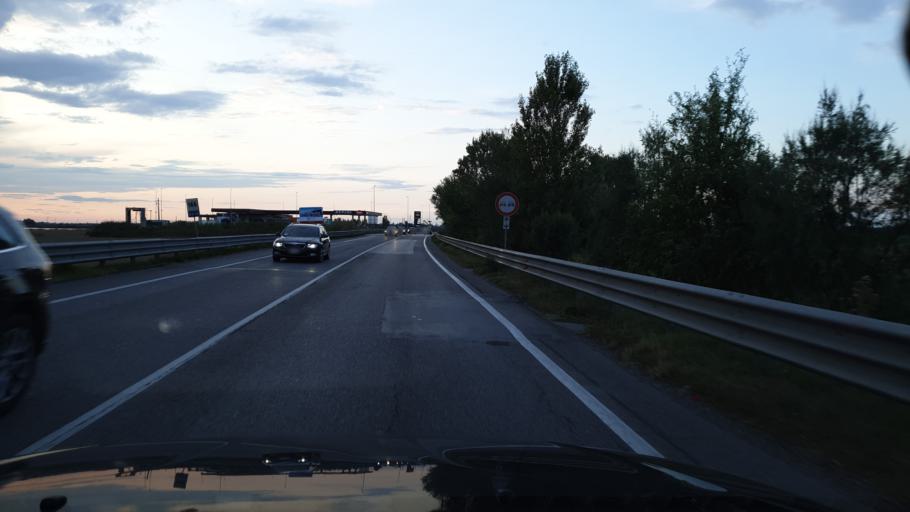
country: IT
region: Emilia-Romagna
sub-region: Provincia di Ravenna
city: Savio
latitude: 44.3080
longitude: 12.2865
